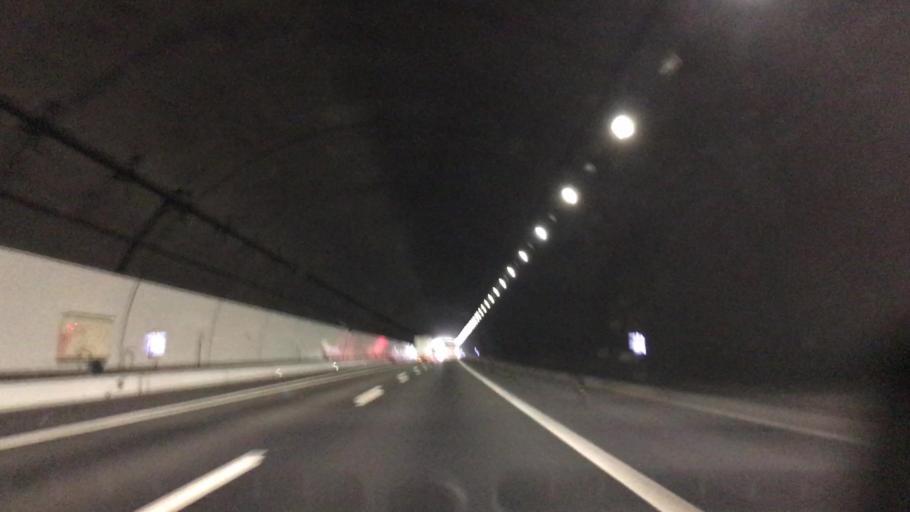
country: JP
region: Shiga Prefecture
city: Kusatsu
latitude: 34.9454
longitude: 136.0271
